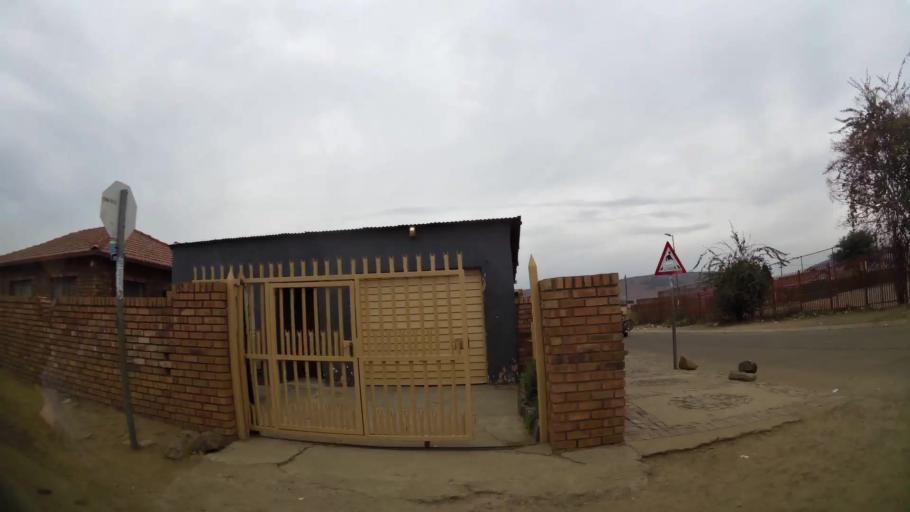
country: ZA
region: Gauteng
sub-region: City of Tshwane Metropolitan Municipality
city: Pretoria
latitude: -25.7140
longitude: 28.3438
